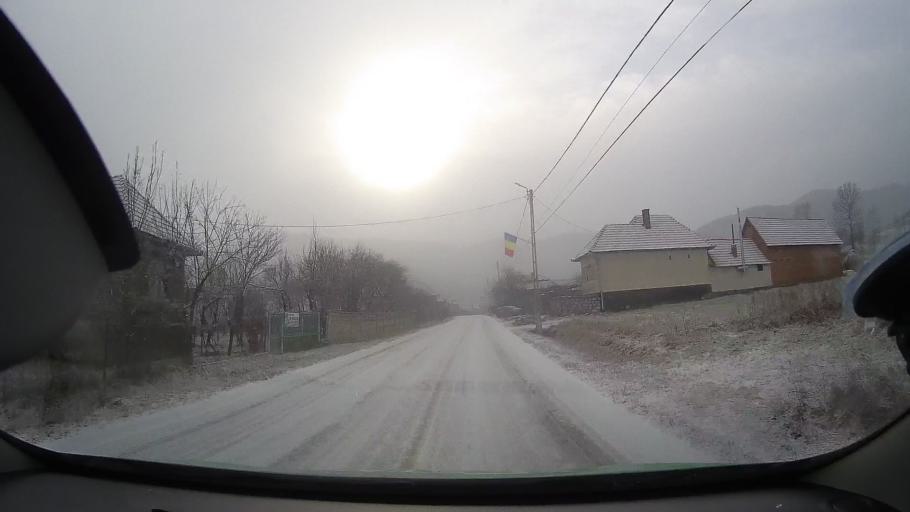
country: RO
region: Alba
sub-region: Comuna Rimetea
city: Rimetea
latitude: 46.3912
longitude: 23.5620
